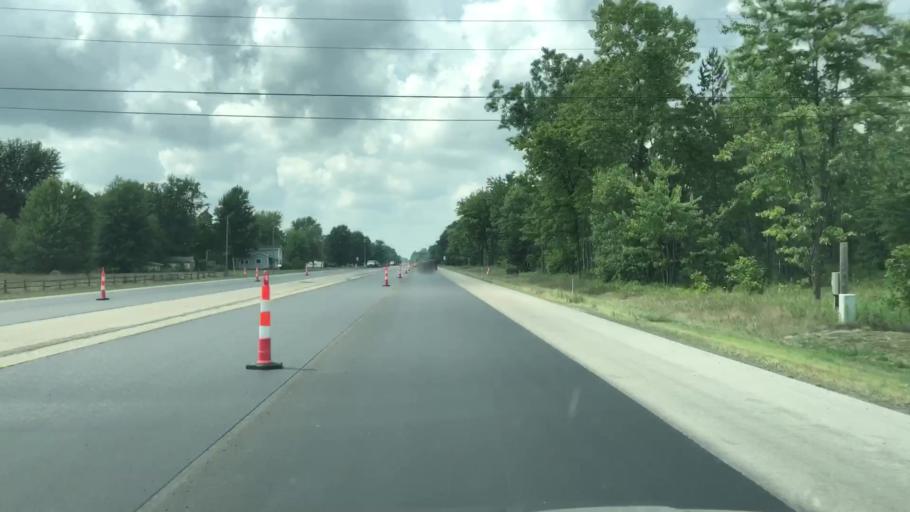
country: US
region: Michigan
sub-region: Isabella County
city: Shepherd
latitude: 43.6120
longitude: -84.6742
